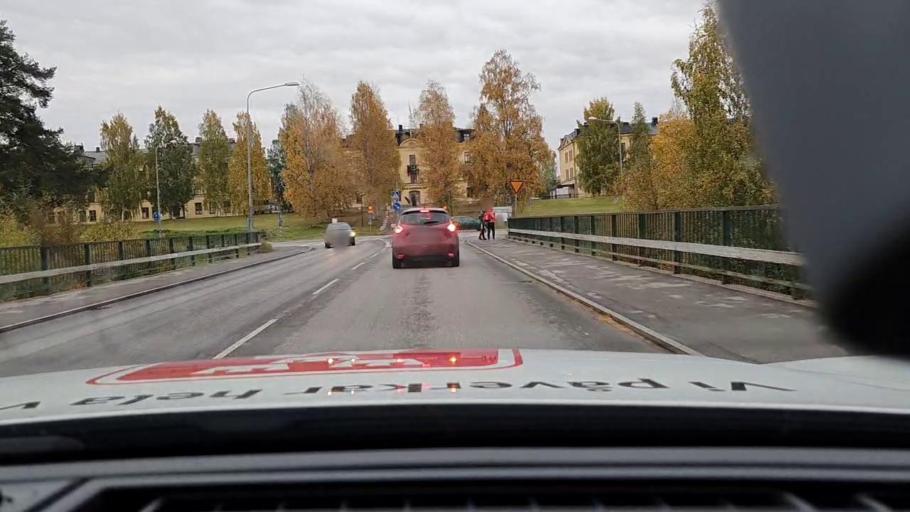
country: SE
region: Norrbotten
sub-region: Bodens Kommun
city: Boden
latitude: 65.8141
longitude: 21.6775
